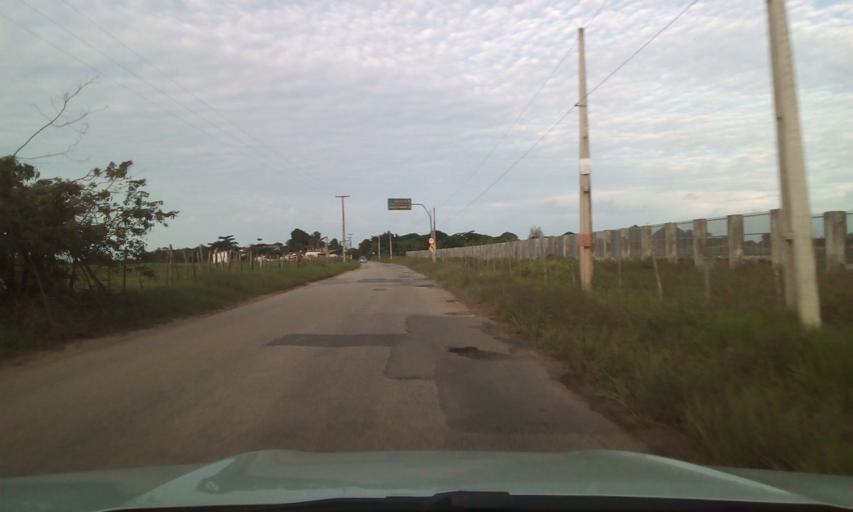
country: BR
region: Paraiba
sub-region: Conde
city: Conde
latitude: -7.2246
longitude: -34.8194
